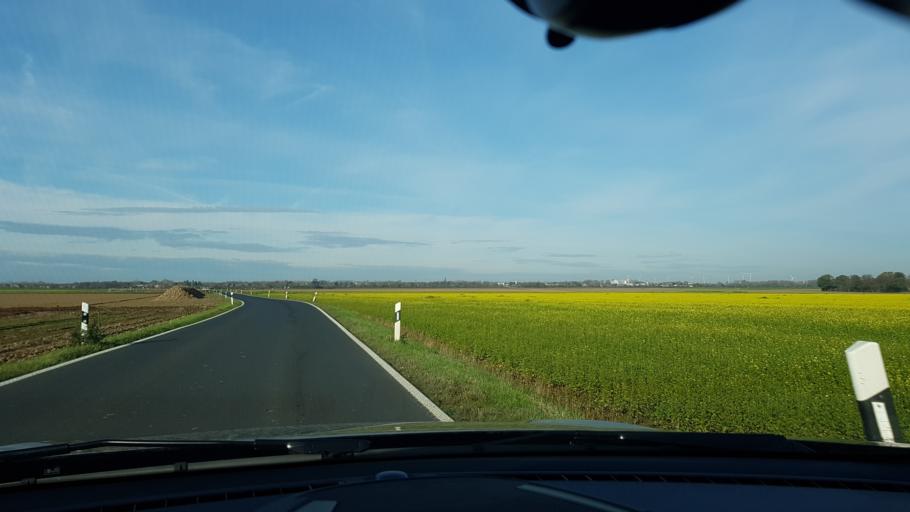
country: DE
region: North Rhine-Westphalia
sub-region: Regierungsbezirk Dusseldorf
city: Neubrueck
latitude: 51.0926
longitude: 6.6442
